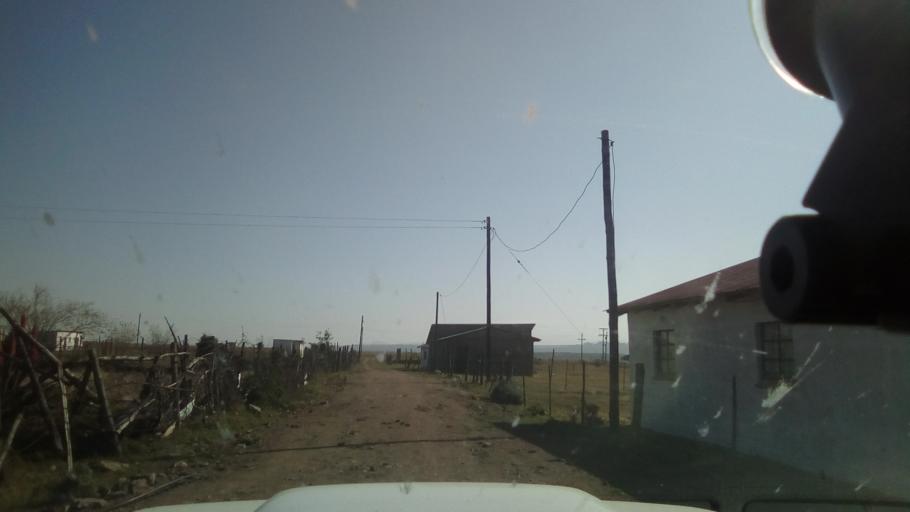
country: ZA
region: Eastern Cape
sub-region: Buffalo City Metropolitan Municipality
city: Bhisho
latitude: -32.9464
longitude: 27.3255
